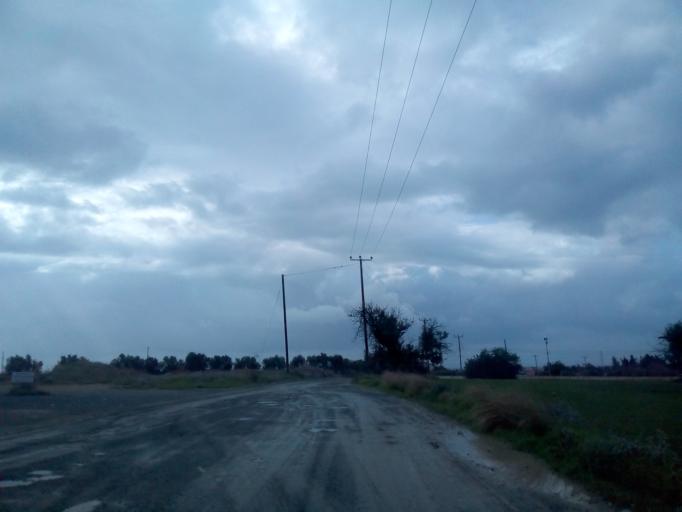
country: CY
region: Limassol
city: Ypsonas
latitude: 34.6749
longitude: 32.9749
